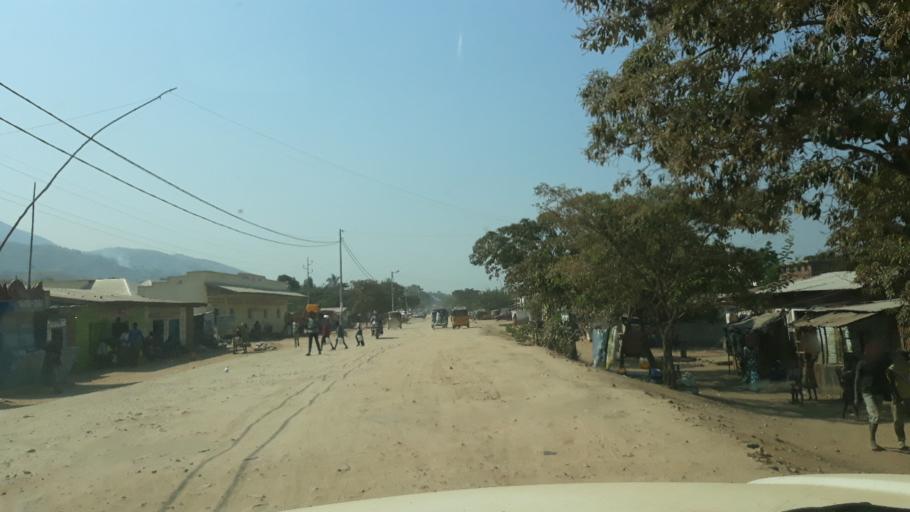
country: CD
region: South Kivu
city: Uvira
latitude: -3.3690
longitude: 29.1473
